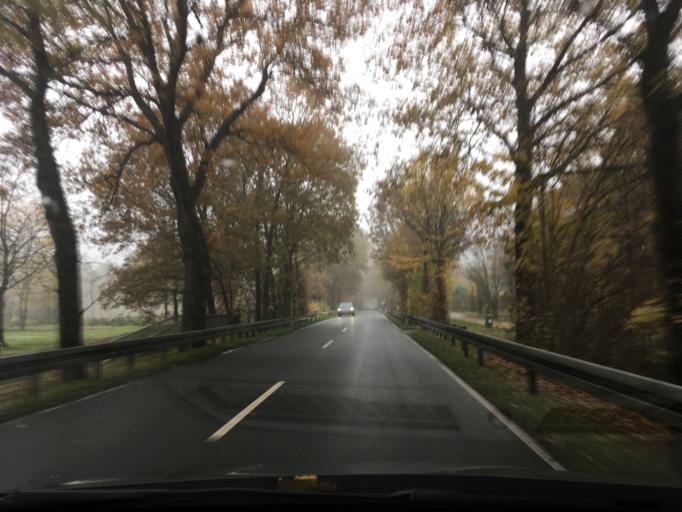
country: DE
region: North Rhine-Westphalia
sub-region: Regierungsbezirk Munster
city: Ahaus
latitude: 52.1115
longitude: 6.9181
